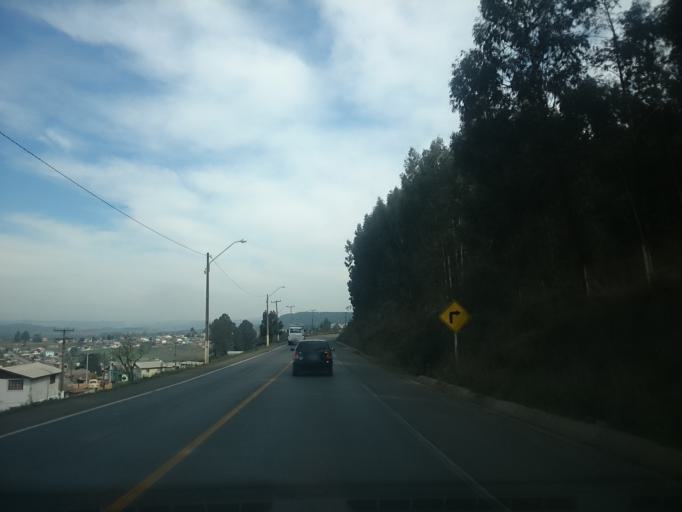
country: BR
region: Santa Catarina
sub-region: Lages
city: Lages
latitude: -27.8354
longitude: -50.3494
